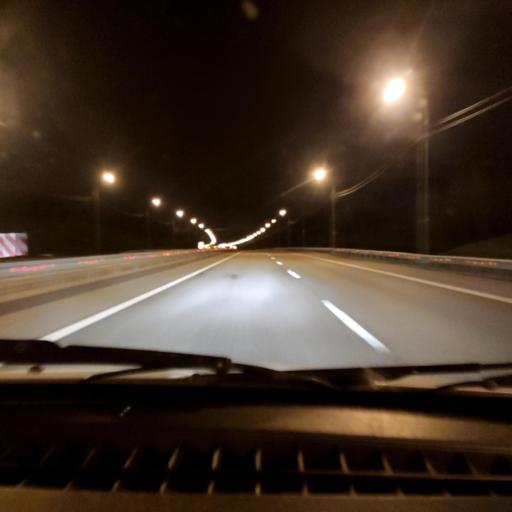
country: RU
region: Lipetsk
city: Zadonsk
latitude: 52.3605
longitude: 38.9369
